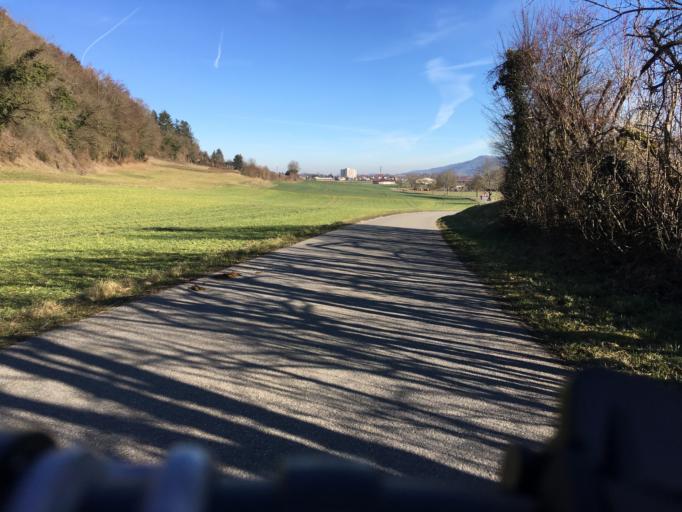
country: CH
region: Schaffhausen
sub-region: Bezirk Stein
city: Ramsen
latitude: 47.7310
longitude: 8.8113
